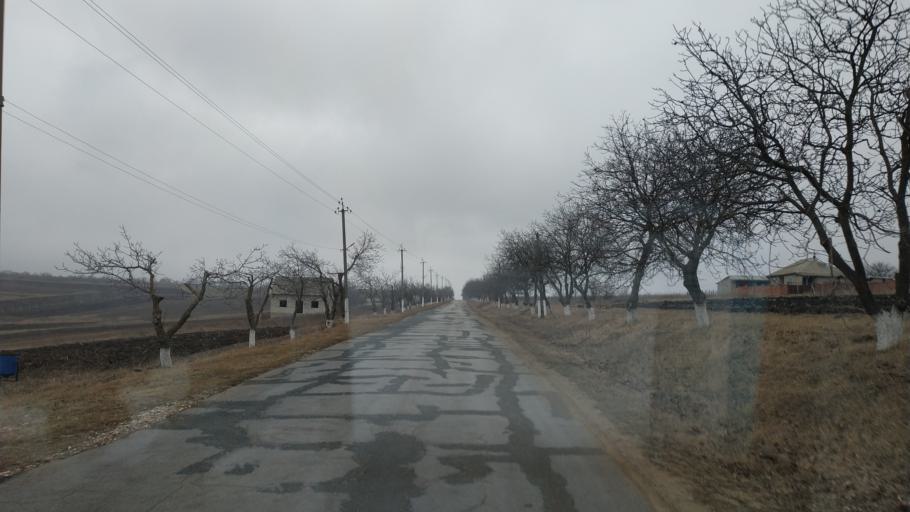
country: MD
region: Laloveni
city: Ialoveni
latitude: 46.8908
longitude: 28.6871
